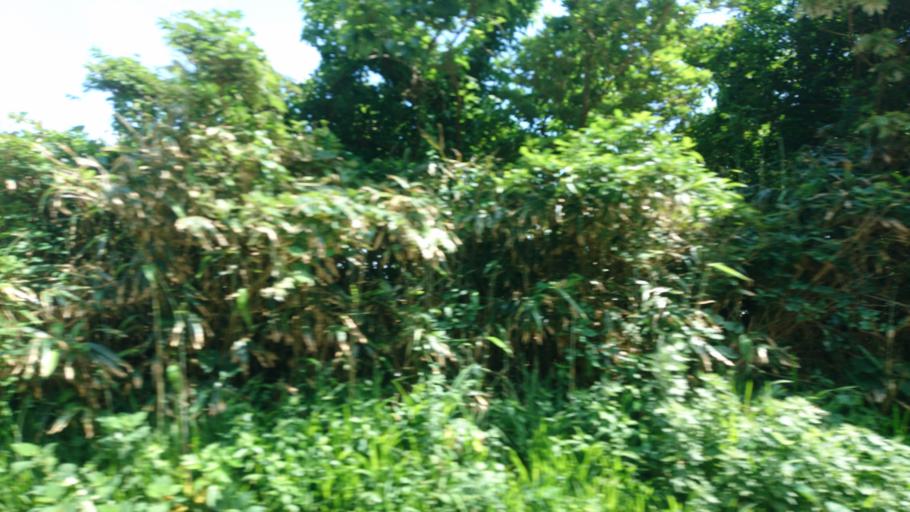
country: JP
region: Shizuoka
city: Shimoda
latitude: 34.3914
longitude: 139.2771
